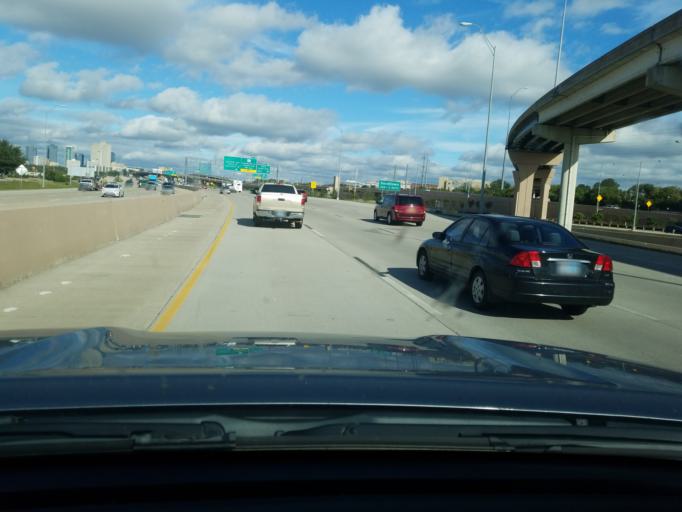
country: US
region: Texas
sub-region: Tarrant County
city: Fort Worth
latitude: 32.7348
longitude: -97.3584
